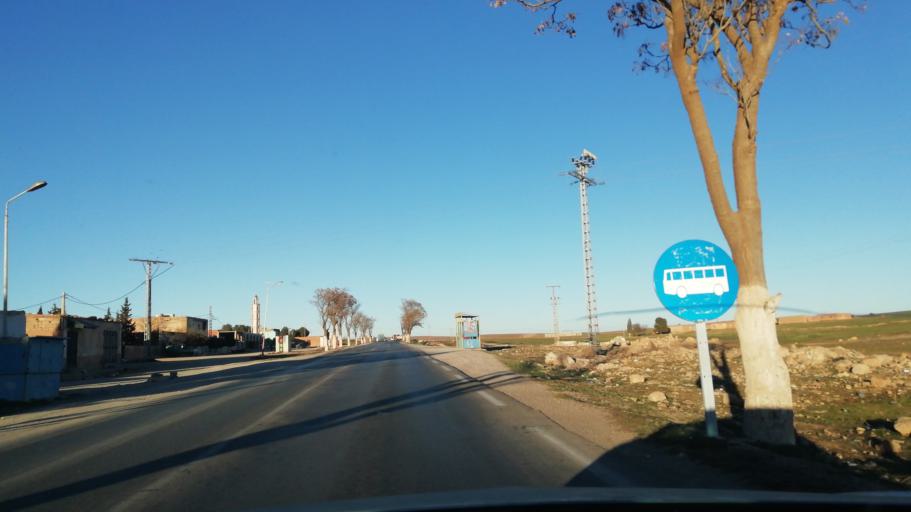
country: DZ
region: Saida
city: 'Ain el Hadjar
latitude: 34.5776
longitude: 0.1292
